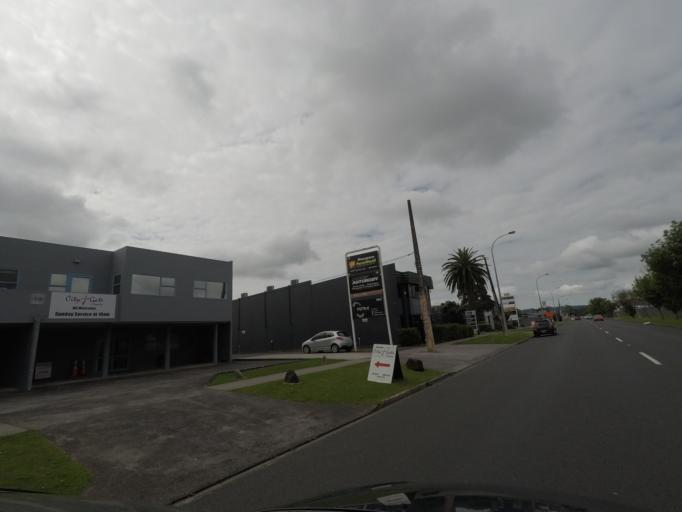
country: NZ
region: Auckland
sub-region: Auckland
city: Waitakere
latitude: -36.8876
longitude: 174.6316
